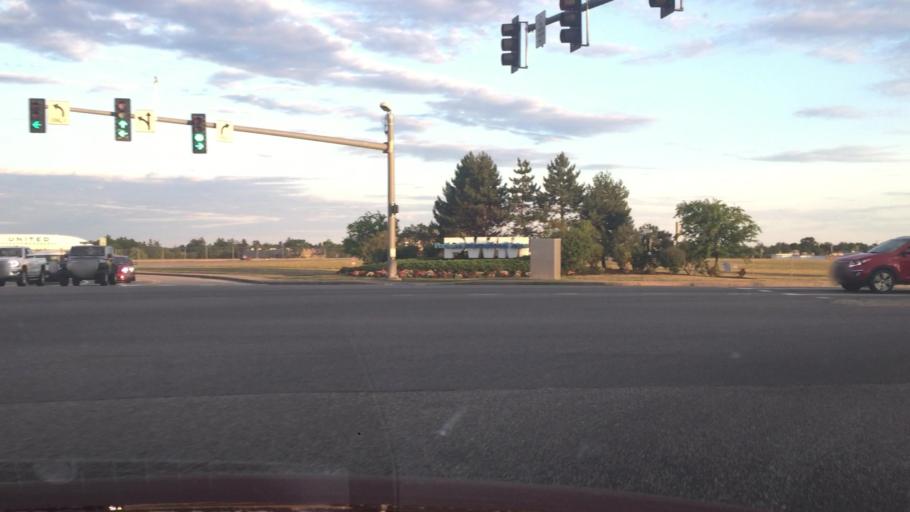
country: US
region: Maine
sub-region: Cumberland County
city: South Portland Gardens
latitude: 43.6483
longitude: -70.3270
